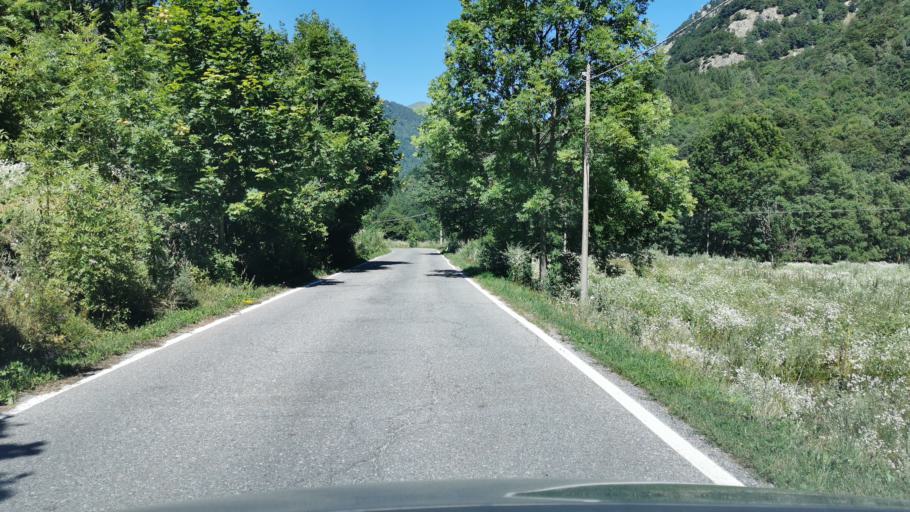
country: IT
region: Piedmont
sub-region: Provincia di Cuneo
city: Entracque
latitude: 44.2352
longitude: 7.3157
